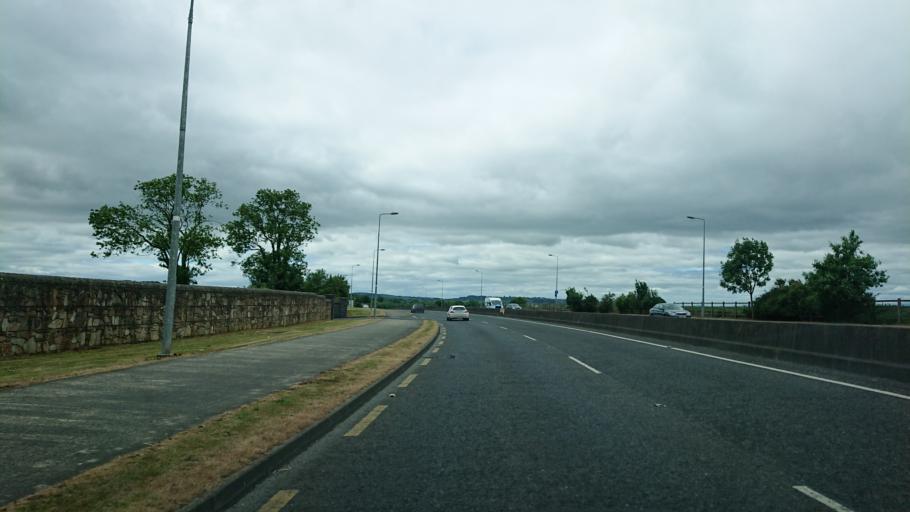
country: IE
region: Munster
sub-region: Waterford
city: Waterford
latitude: 52.2361
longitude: -7.0990
